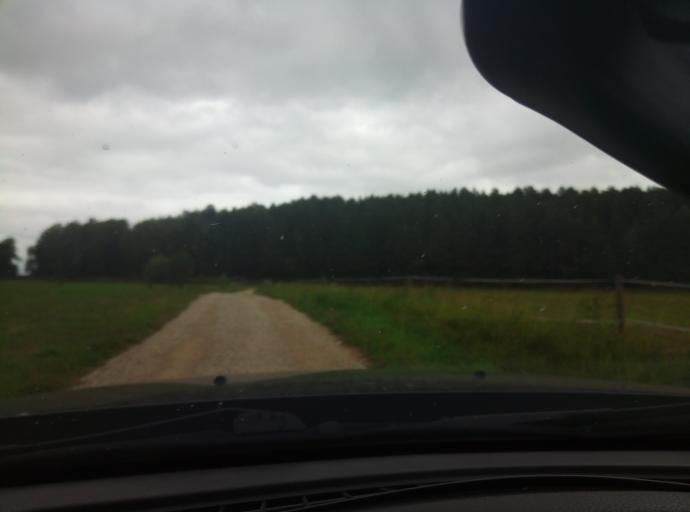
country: RU
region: Kaluga
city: Zhukovo
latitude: 54.9545
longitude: 36.7635
